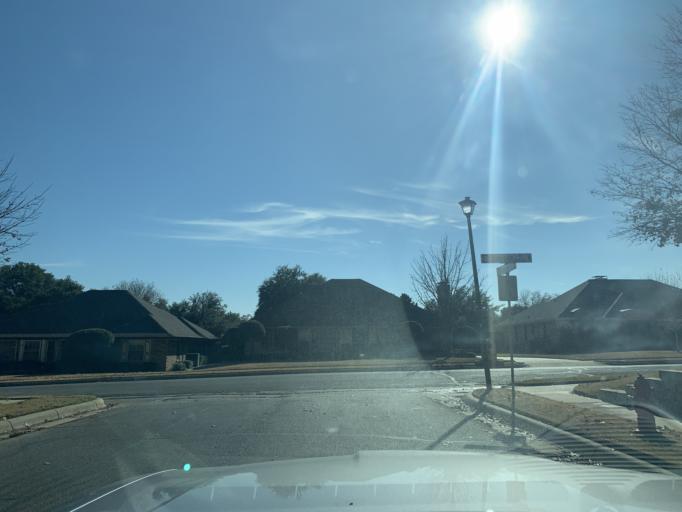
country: US
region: Texas
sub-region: Tarrant County
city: Bedford
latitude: 32.8463
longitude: -97.1561
